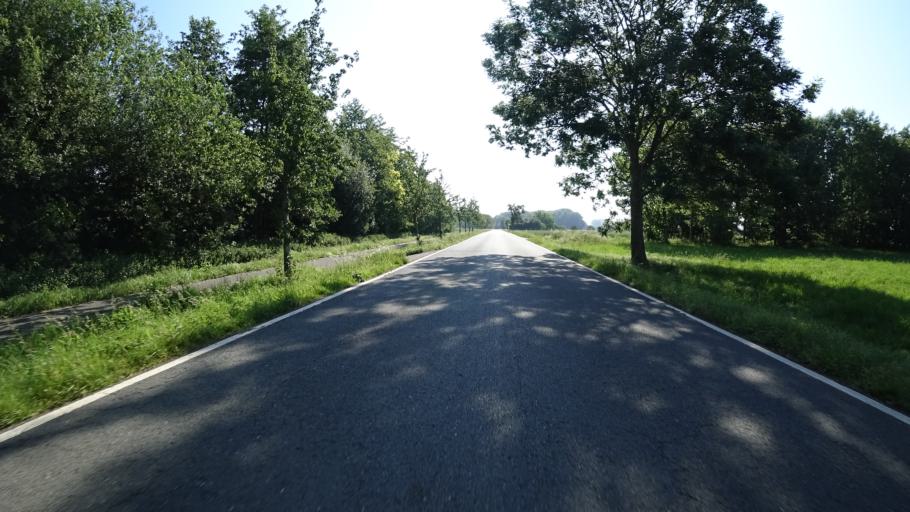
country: DE
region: North Rhine-Westphalia
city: Erwitte
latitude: 51.6322
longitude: 8.3775
